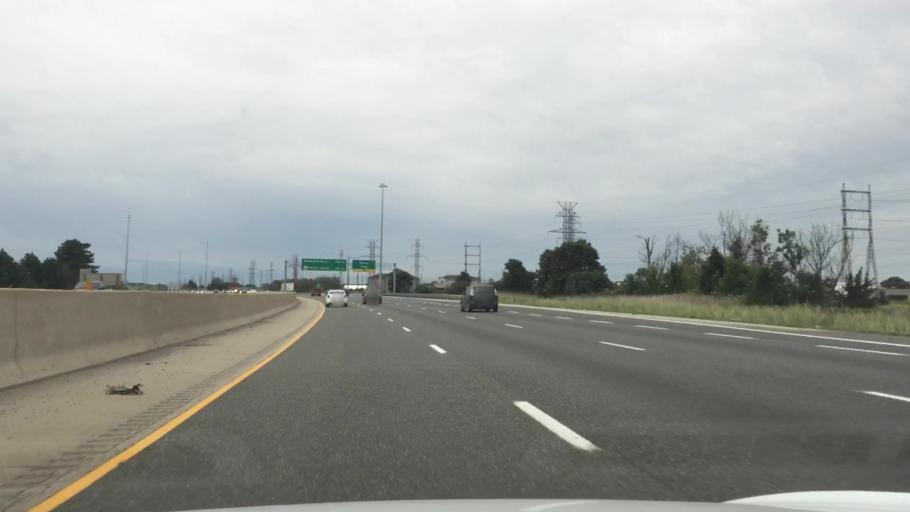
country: CA
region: Ontario
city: London
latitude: 42.9310
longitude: -81.2006
